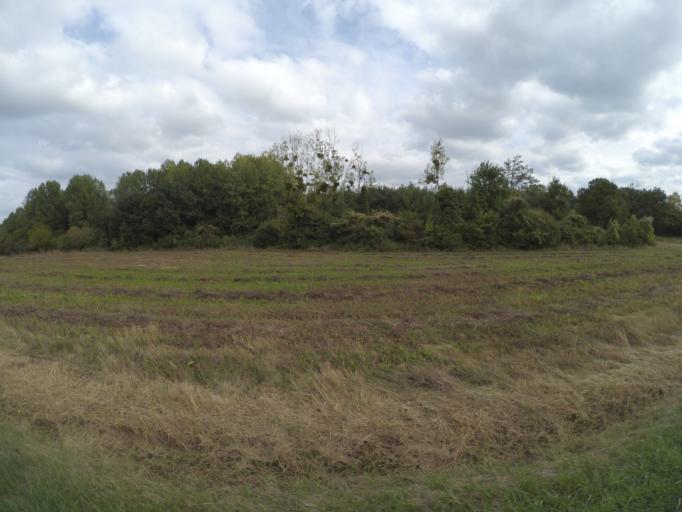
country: FR
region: Centre
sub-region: Departement d'Indre-et-Loire
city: Vernou-sur-Brenne
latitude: 47.4461
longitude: 0.8651
